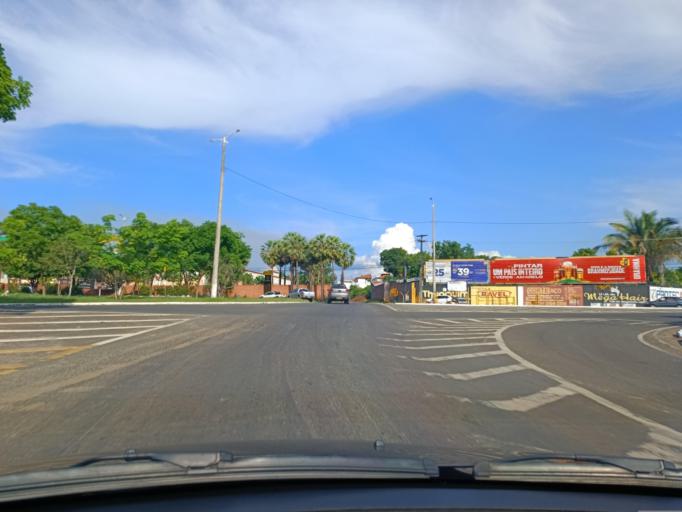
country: BR
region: Piaui
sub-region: Teresina
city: Teresina
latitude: -5.0828
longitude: -42.7507
